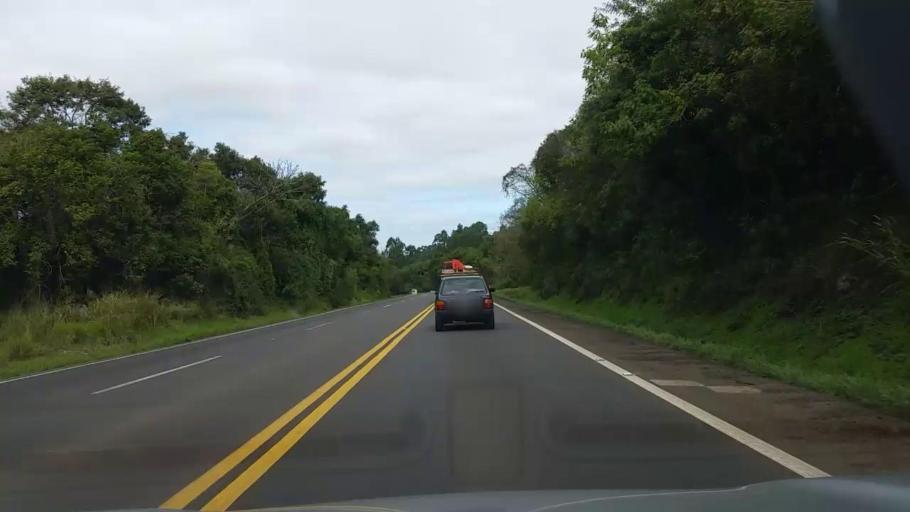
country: BR
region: Rio Grande do Sul
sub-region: Arroio Do Meio
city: Arroio do Meio
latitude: -29.3921
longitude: -52.0422
